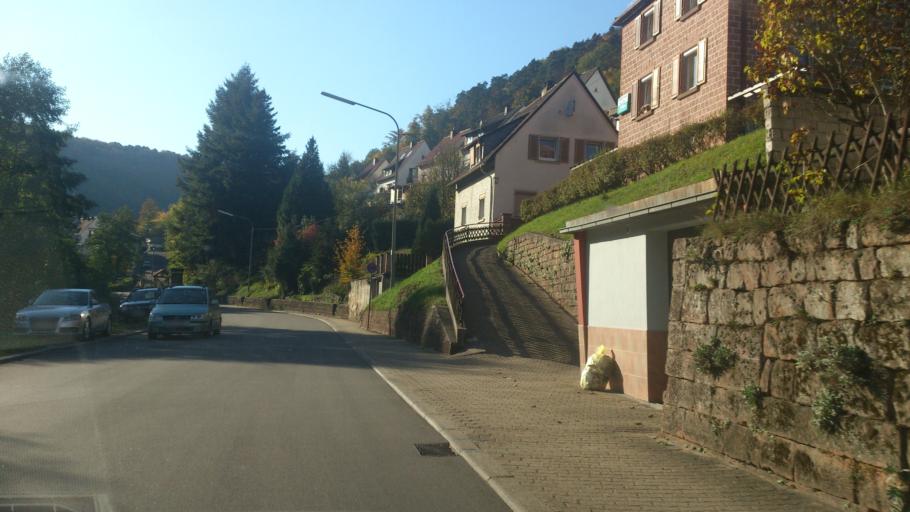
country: DE
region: Rheinland-Pfalz
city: Frankeneck
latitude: 49.3696
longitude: 8.0404
